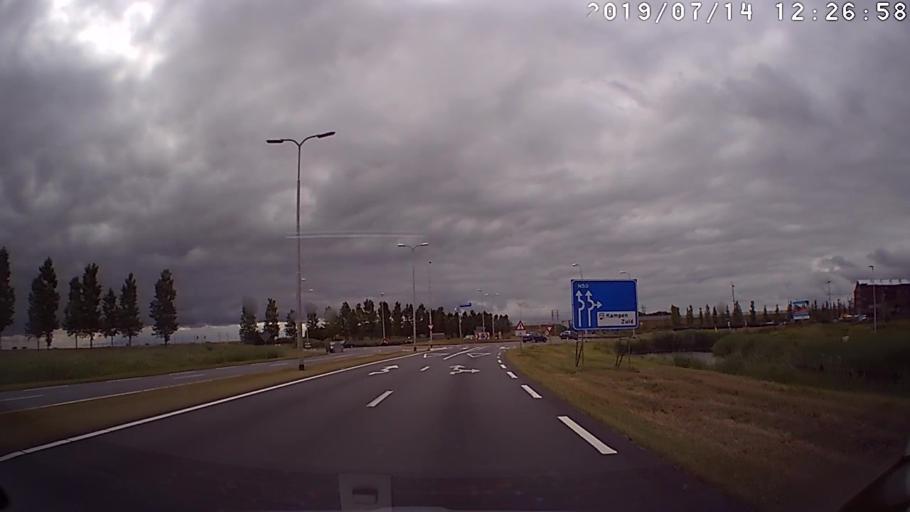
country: NL
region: Overijssel
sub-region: Gemeente Kampen
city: Kampen
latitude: 52.5341
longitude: 5.9197
